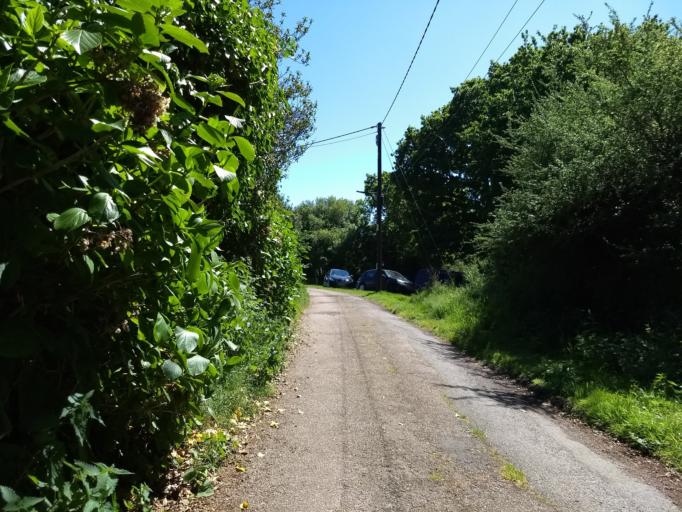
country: GB
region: England
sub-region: Isle of Wight
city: Seaview
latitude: 50.6979
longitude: -1.1169
